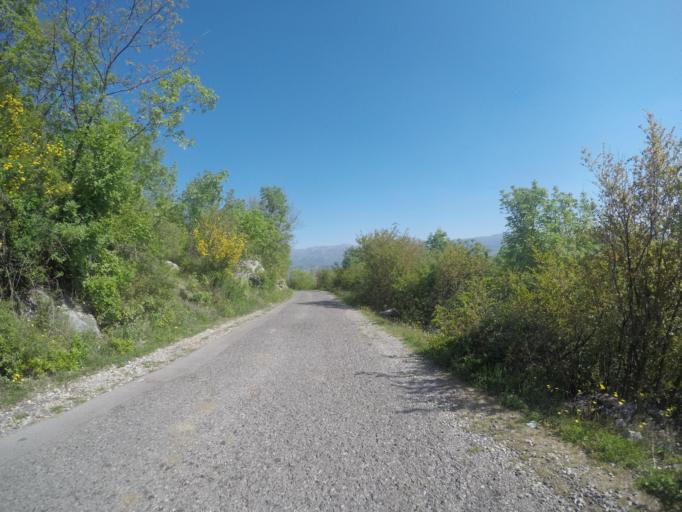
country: ME
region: Danilovgrad
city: Danilovgrad
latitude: 42.5156
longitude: 19.0983
